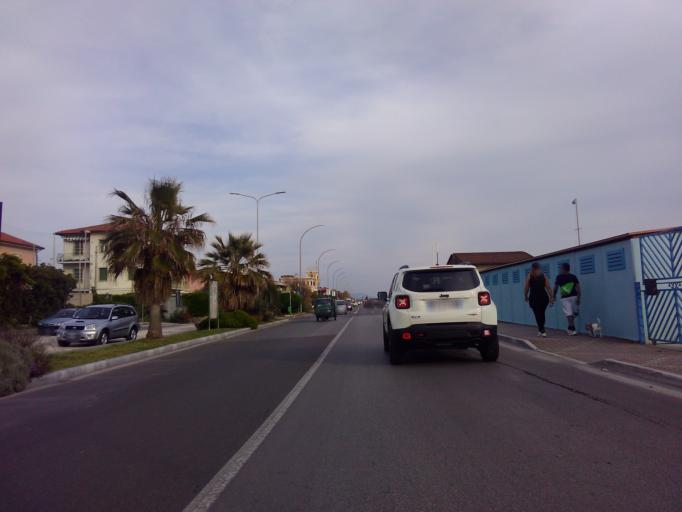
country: IT
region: Tuscany
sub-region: Provincia di Massa-Carrara
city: Massa
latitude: 44.0109
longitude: 10.0942
